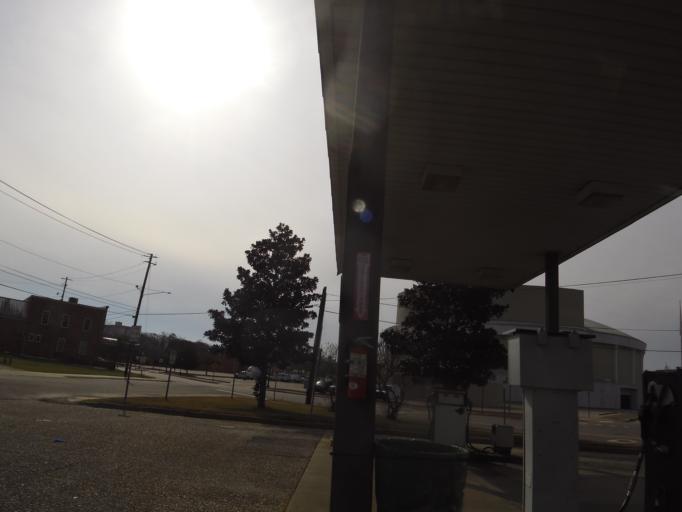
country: US
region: Alabama
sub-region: Houston County
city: Dothan
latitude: 31.2255
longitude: -85.3888
